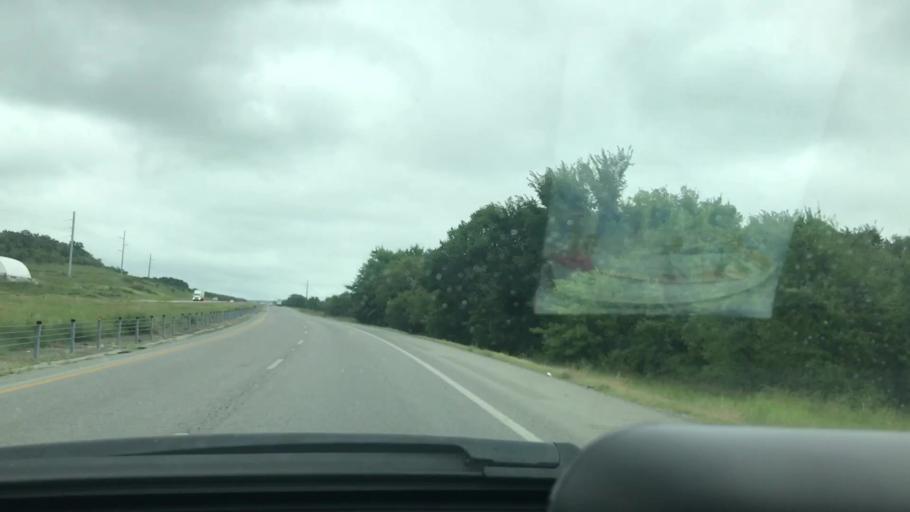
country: US
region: Oklahoma
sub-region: Coal County
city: Coalgate
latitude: 34.6488
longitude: -95.9431
